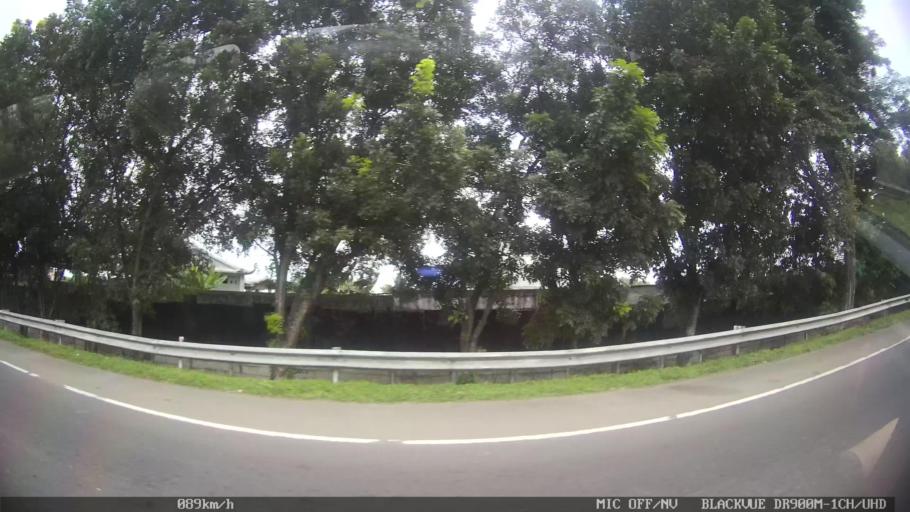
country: ID
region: North Sumatra
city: Labuhan Deli
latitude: 3.6830
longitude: 98.6809
